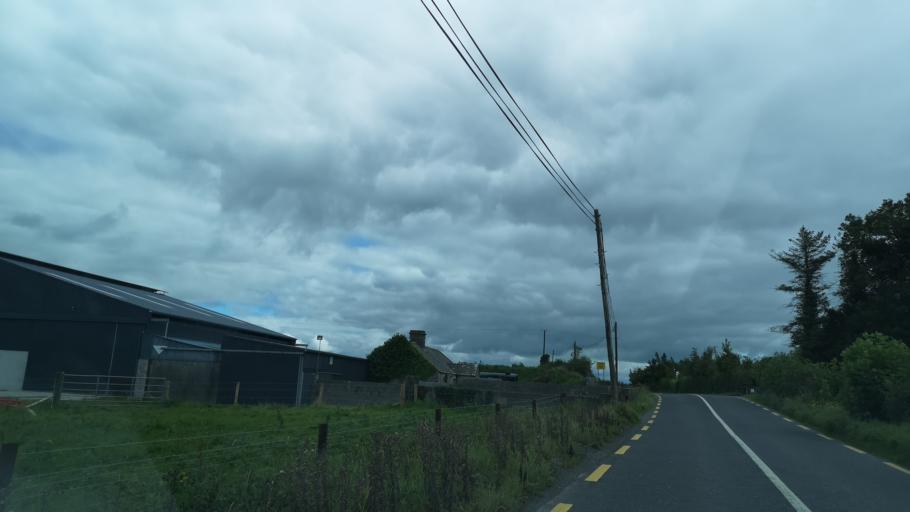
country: IE
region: Connaught
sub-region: County Galway
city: Ballinasloe
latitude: 53.3070
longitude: -8.1467
